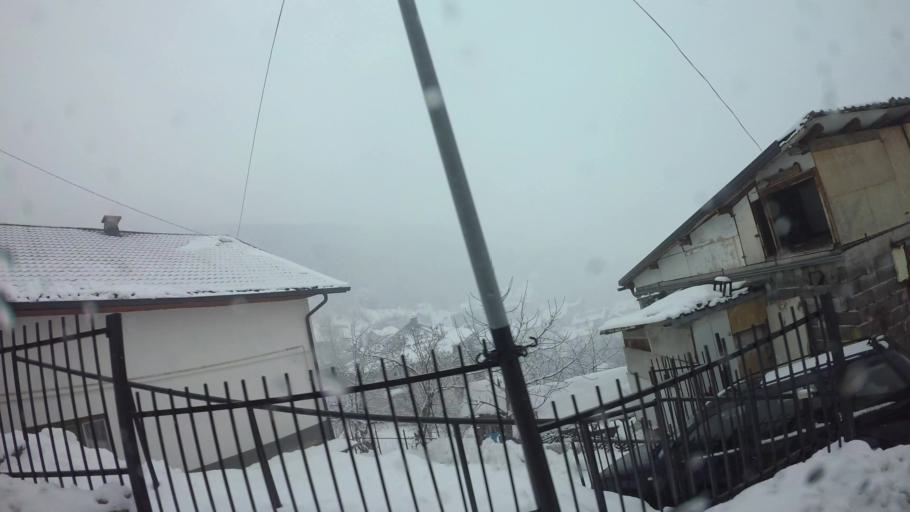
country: BA
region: Federation of Bosnia and Herzegovina
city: Kobilja Glava
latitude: 43.8458
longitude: 18.4290
